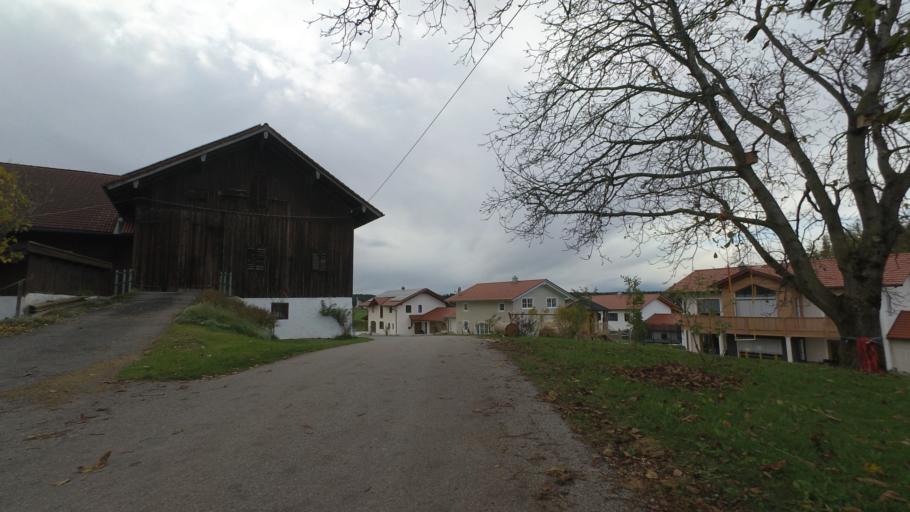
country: DE
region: Bavaria
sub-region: Upper Bavaria
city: Nussdorf
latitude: 47.9095
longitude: 12.5928
